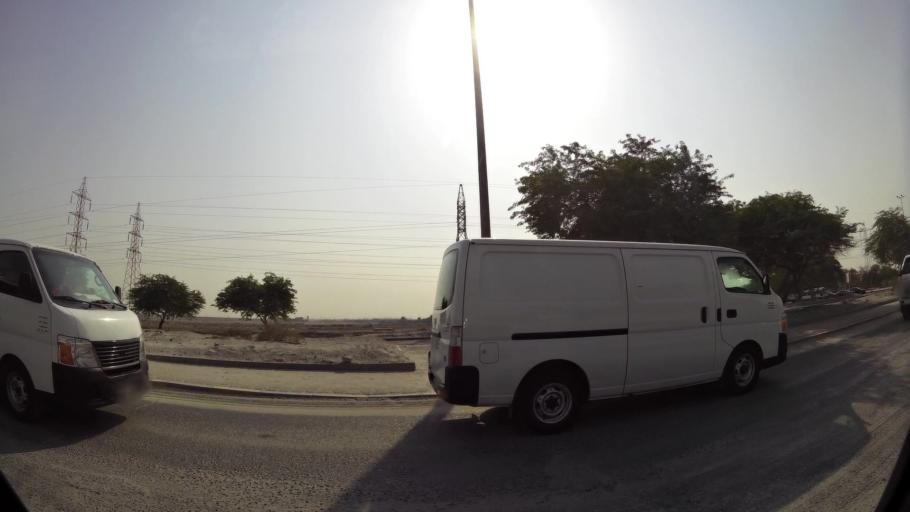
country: KW
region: Al Asimah
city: Ar Rabiyah
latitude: 29.2789
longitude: 47.8426
